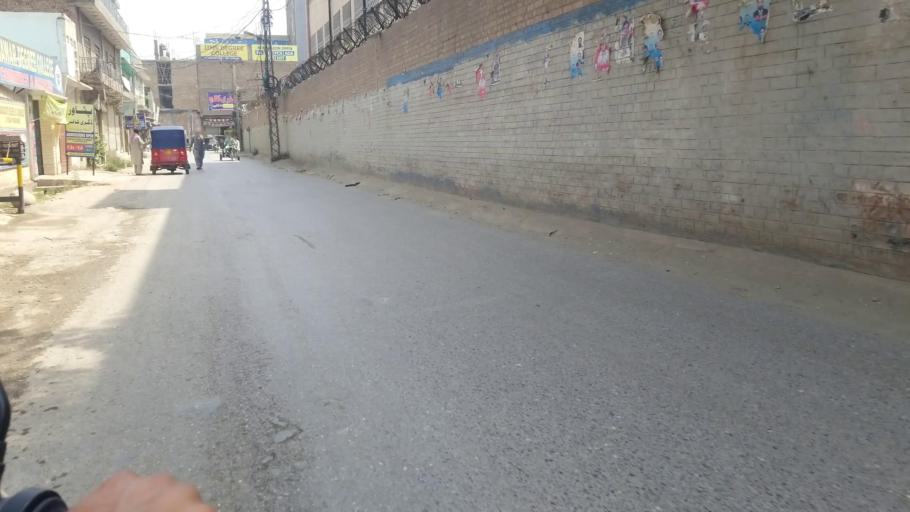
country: PK
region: Khyber Pakhtunkhwa
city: Peshawar
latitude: 34.0232
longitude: 71.5776
